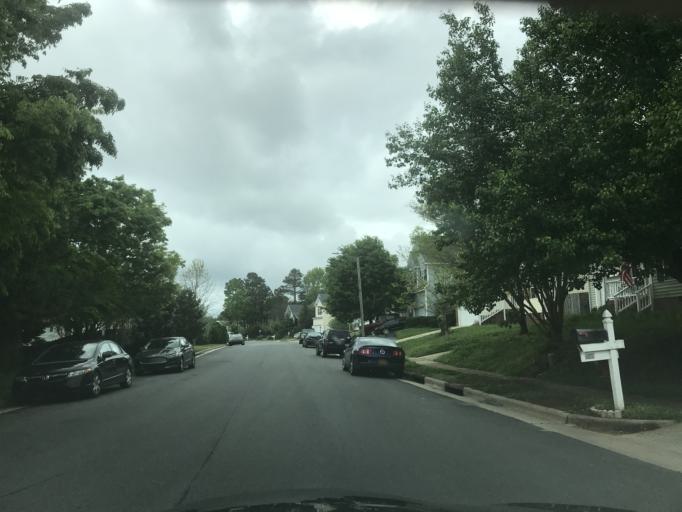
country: US
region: North Carolina
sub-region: Wake County
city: West Raleigh
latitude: 35.7453
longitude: -78.6838
